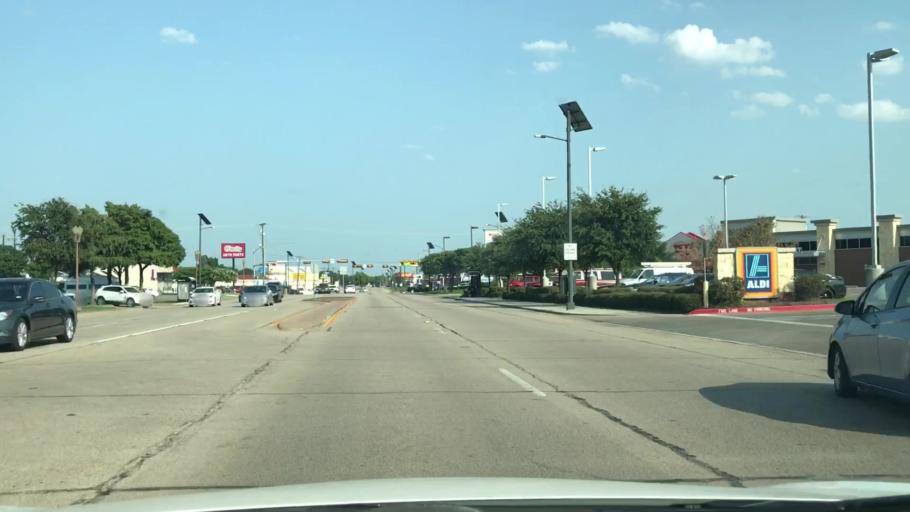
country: US
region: Texas
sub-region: Dallas County
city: Irving
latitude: 32.8124
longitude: -96.9360
